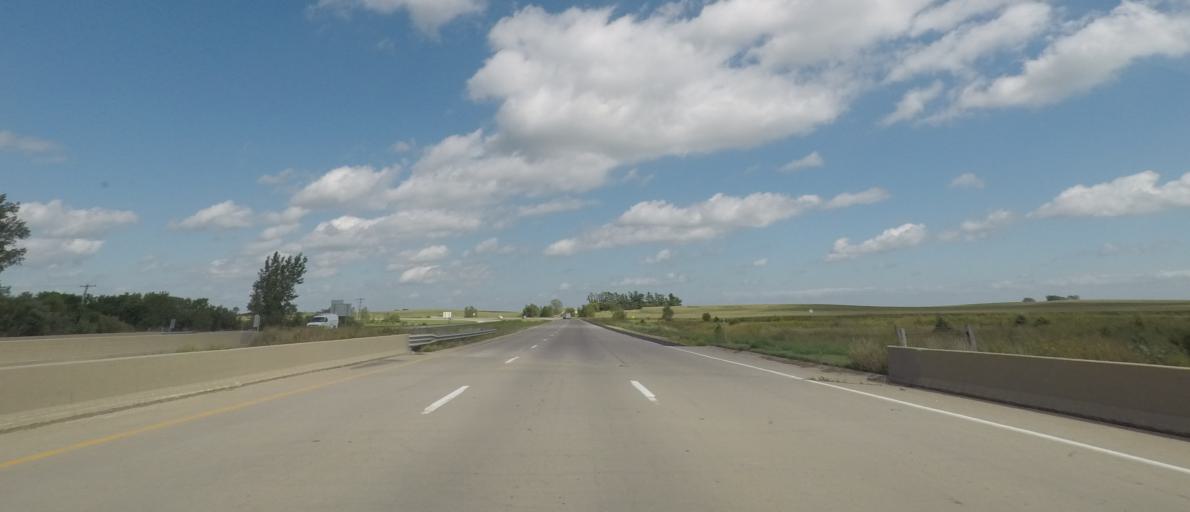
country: US
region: Iowa
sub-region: Jones County
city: Monticello
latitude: 42.2078
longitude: -91.1824
